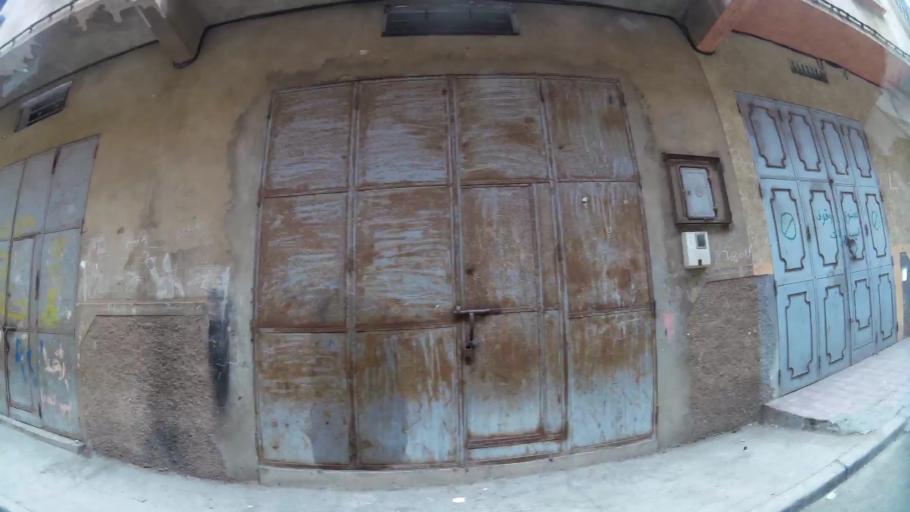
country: MA
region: Rabat-Sale-Zemmour-Zaer
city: Sale
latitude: 34.0589
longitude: -6.7807
